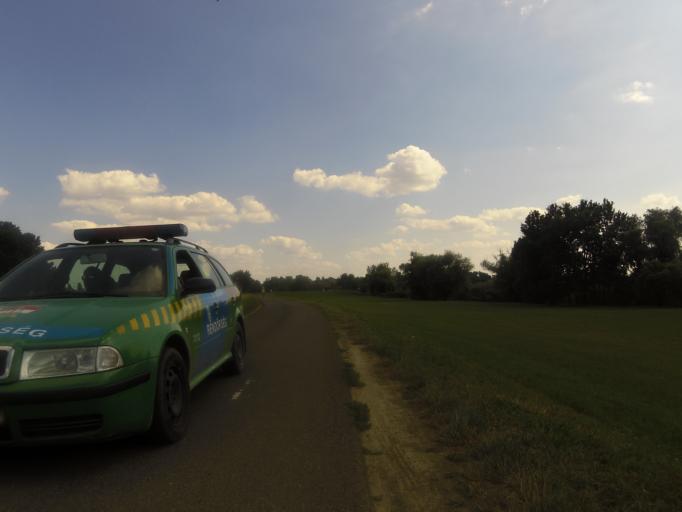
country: HU
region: Jasz-Nagykun-Szolnok
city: Tiszafured
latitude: 47.6157
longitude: 20.7257
